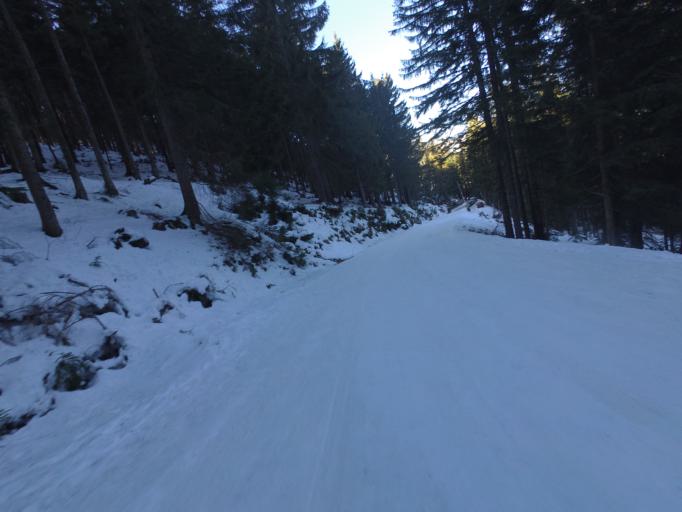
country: AT
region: Salzburg
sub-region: Politischer Bezirk Hallein
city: Scheffau am Tennengebirge
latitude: 47.6409
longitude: 13.2462
